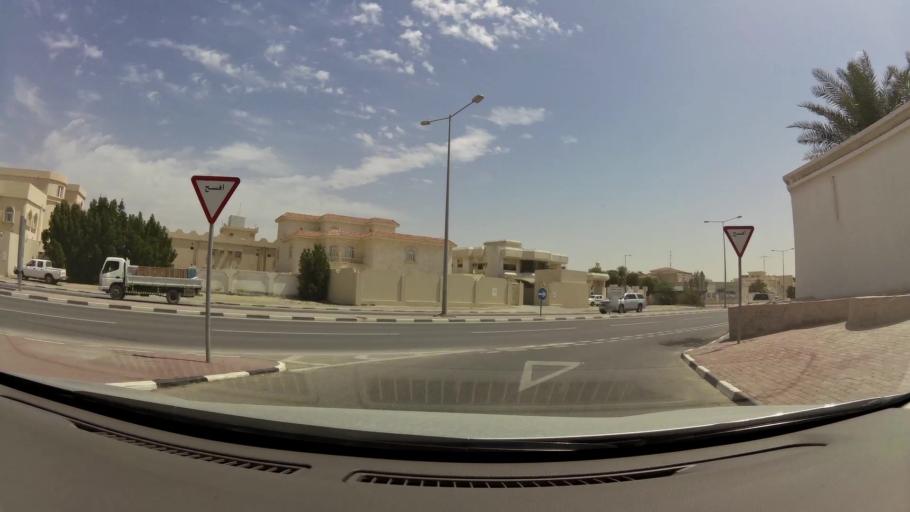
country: QA
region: Baladiyat ar Rayyan
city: Ar Rayyan
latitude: 25.2836
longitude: 51.4202
